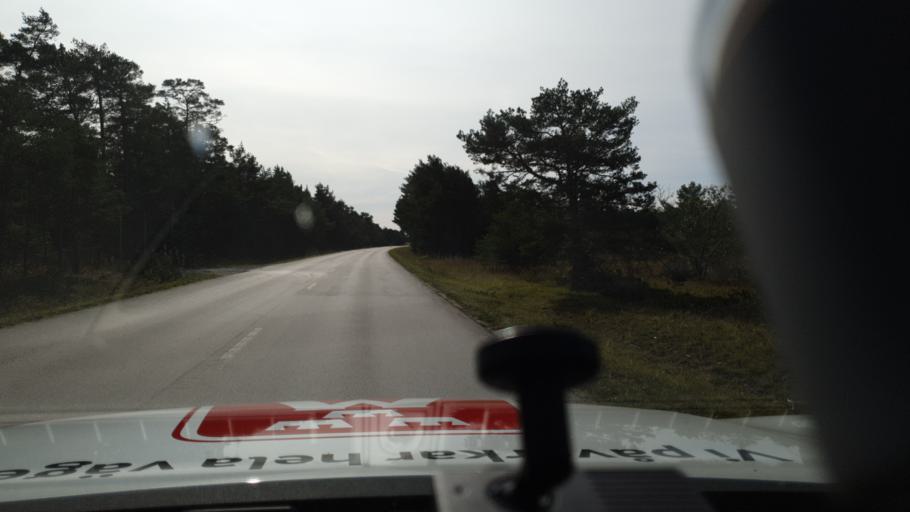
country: SE
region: Gotland
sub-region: Gotland
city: Slite
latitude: 57.8851
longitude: 19.0890
